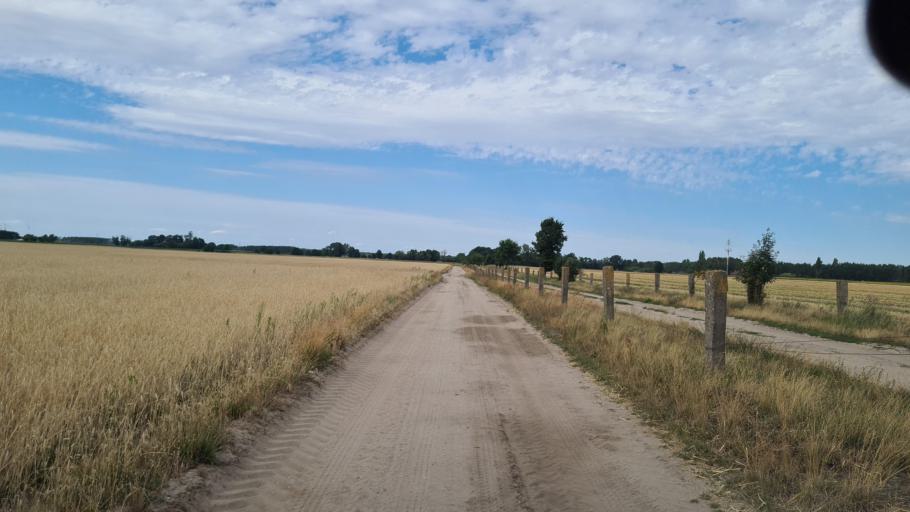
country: DE
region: Saxony-Anhalt
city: Holzdorf
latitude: 51.8013
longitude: 13.1796
